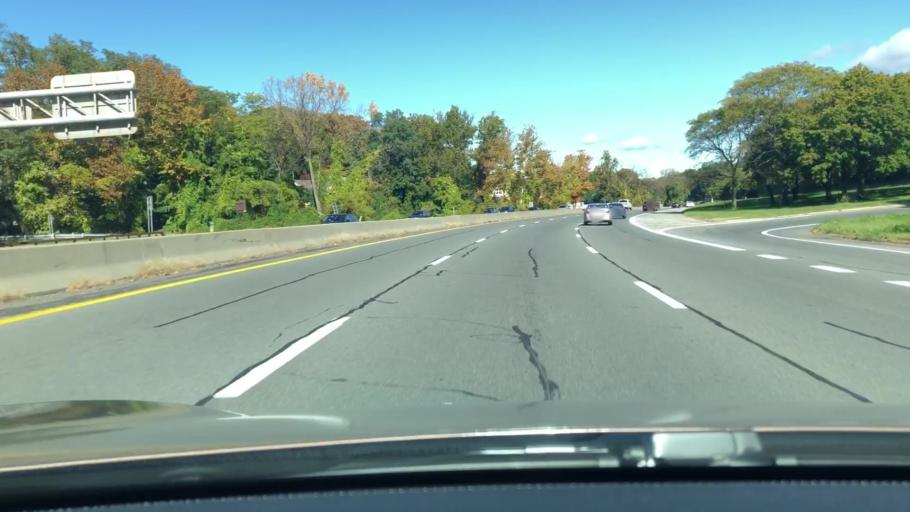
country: US
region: New York
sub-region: Westchester County
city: Bronxville
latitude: 40.9527
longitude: -73.8532
